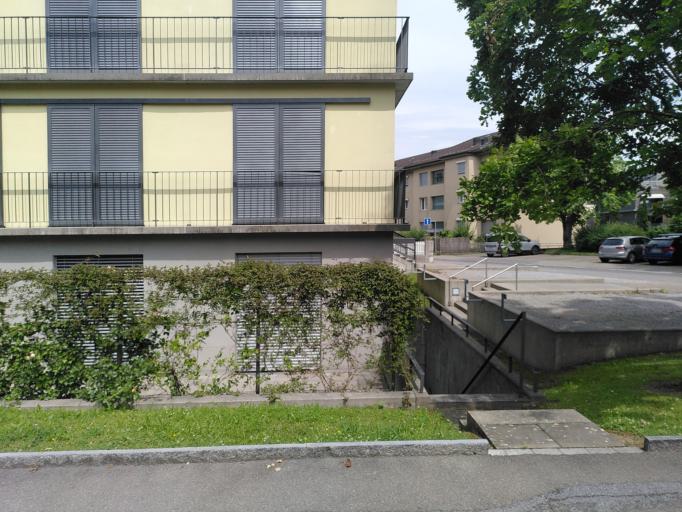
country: CH
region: Zurich
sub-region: Bezirk Horgen
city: Thalwil
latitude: 47.2915
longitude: 8.5635
